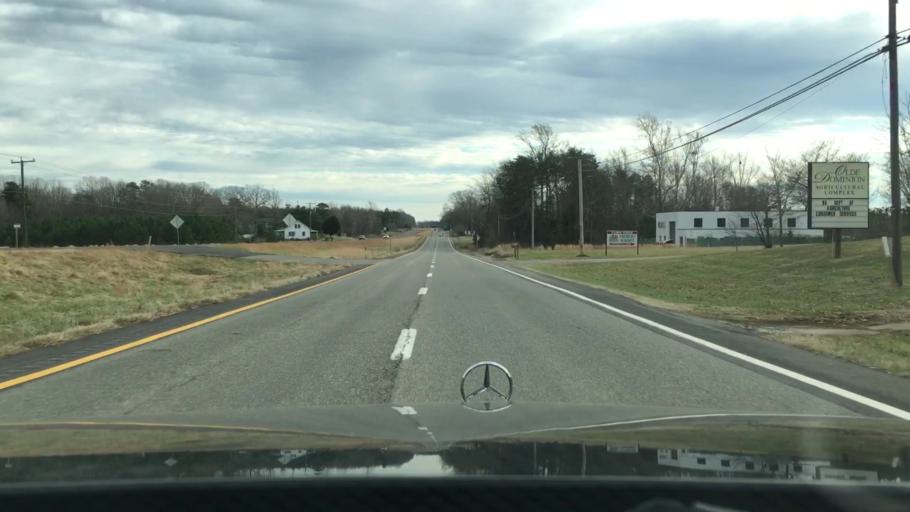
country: US
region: Virginia
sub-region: Pittsylvania County
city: Chatham
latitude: 36.8630
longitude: -79.4017
